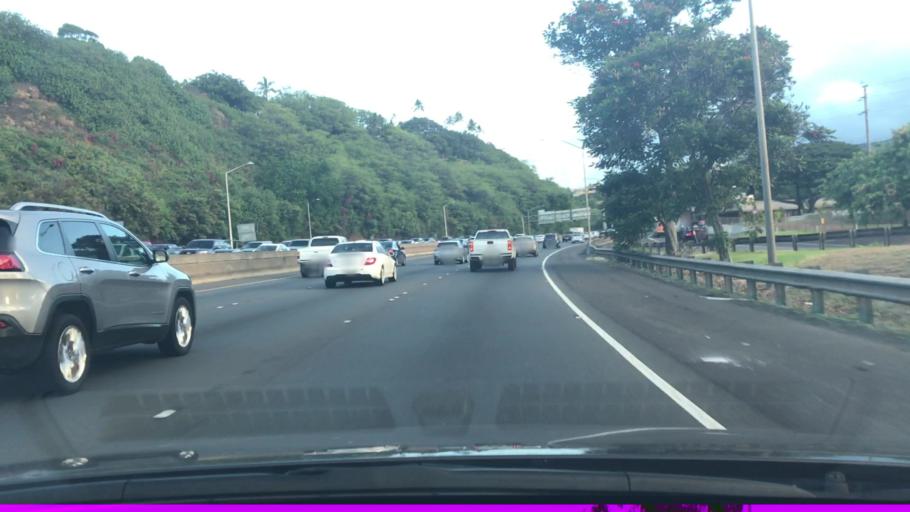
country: US
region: Hawaii
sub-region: Honolulu County
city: Halawa Heights
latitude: 21.3499
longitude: -157.8961
